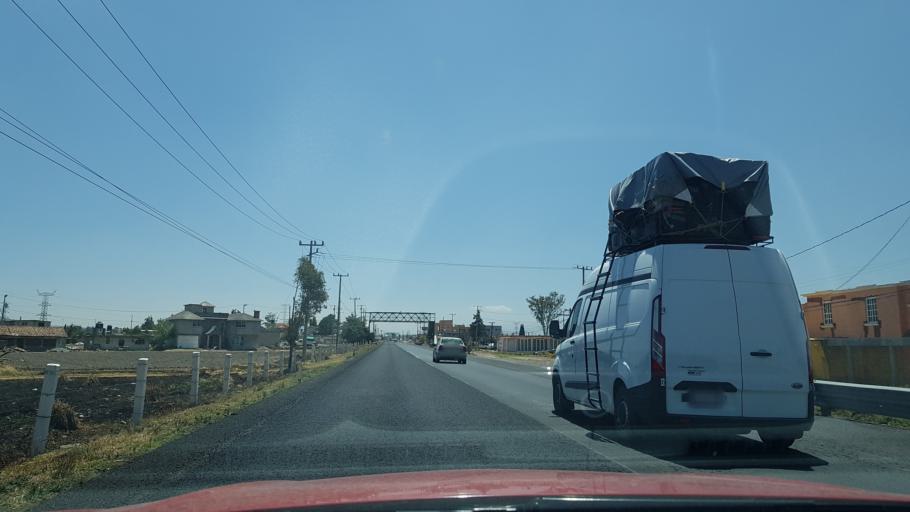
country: MX
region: Mexico
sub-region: Ixtlahuaca
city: Santo Domingo de Guzman
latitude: 19.5918
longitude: -99.7711
